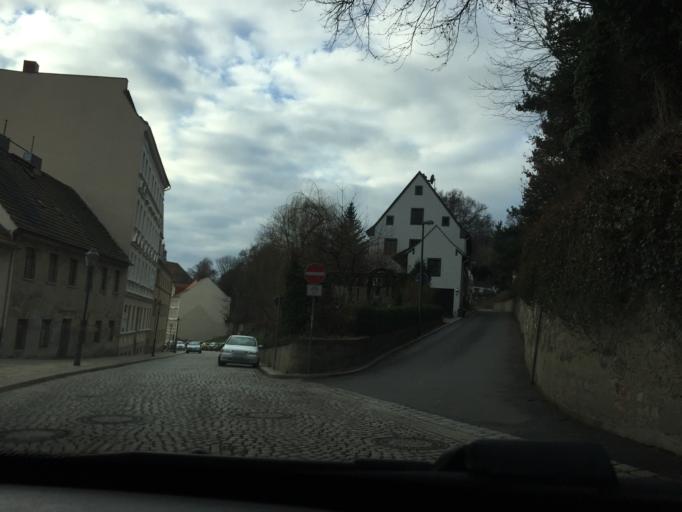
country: DE
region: Saxony
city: Goerlitz
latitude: 51.1623
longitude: 14.9917
